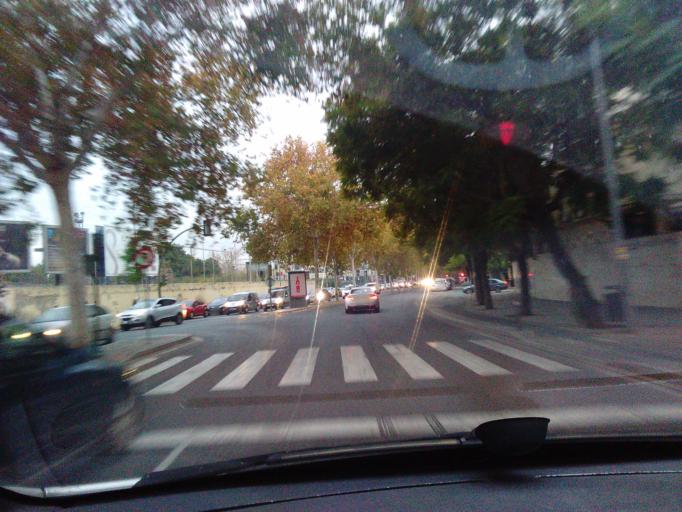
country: ES
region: Andalusia
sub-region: Provincia de Sevilla
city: Sevilla
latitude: 37.3776
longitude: -5.9664
